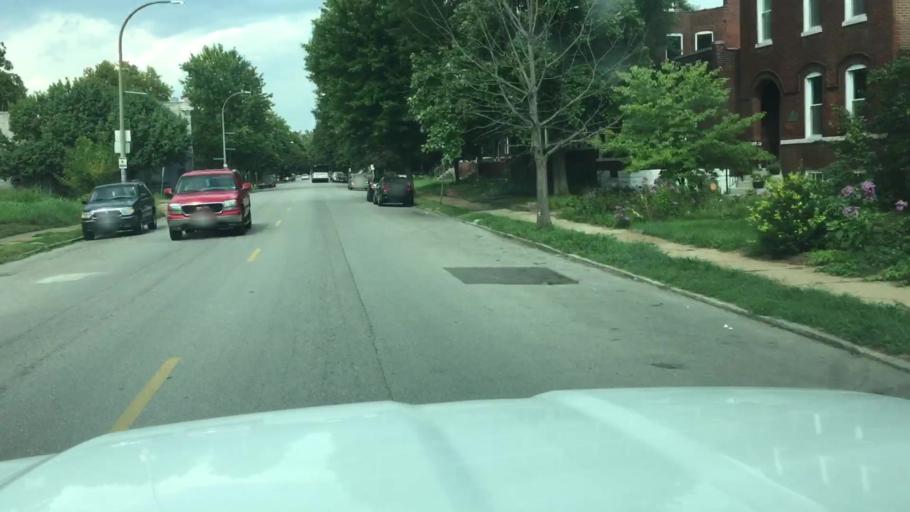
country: US
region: Missouri
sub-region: Saint Louis County
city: Lemay
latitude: 38.5600
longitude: -90.2485
